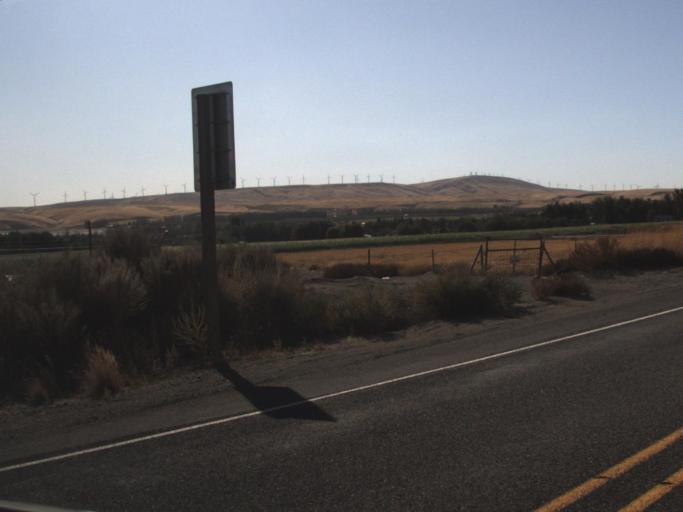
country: US
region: Washington
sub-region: Benton County
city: Finley
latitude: 46.1478
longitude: -119.0143
